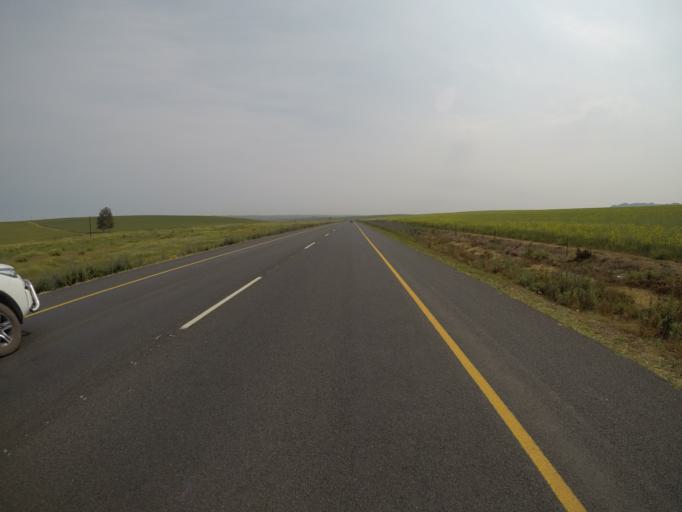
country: ZA
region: Western Cape
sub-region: West Coast District Municipality
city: Malmesbury
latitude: -33.4669
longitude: 18.7907
